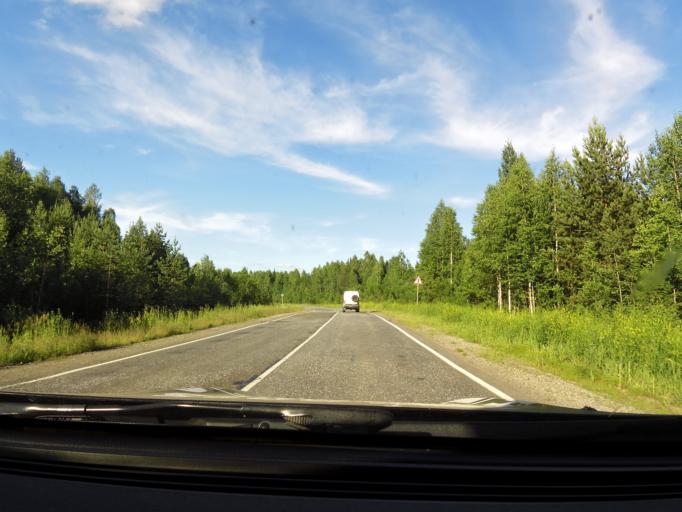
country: RU
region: Kirov
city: Belorechensk
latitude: 58.7575
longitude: 52.3529
